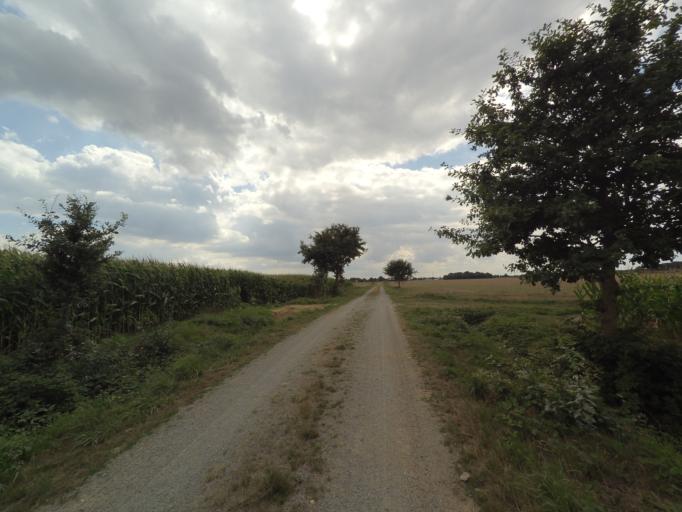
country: FR
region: Pays de la Loire
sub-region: Departement de la Loire-Atlantique
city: Vieillevigne
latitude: 46.9815
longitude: -1.4130
